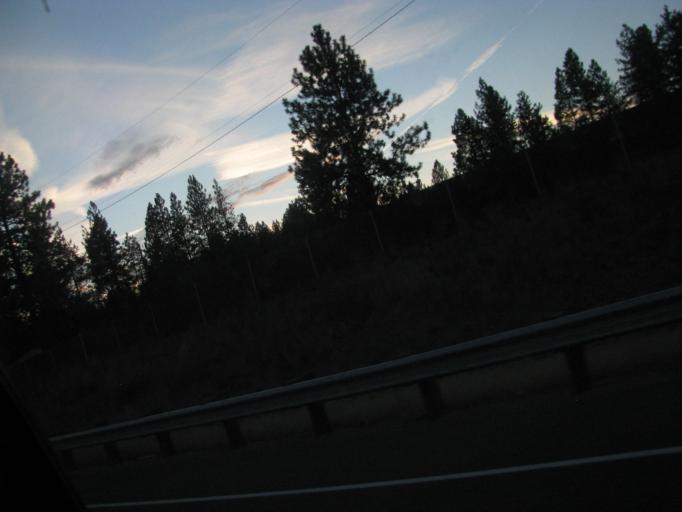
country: US
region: Washington
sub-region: Spokane County
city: Mead
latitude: 47.7812
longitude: -117.3572
